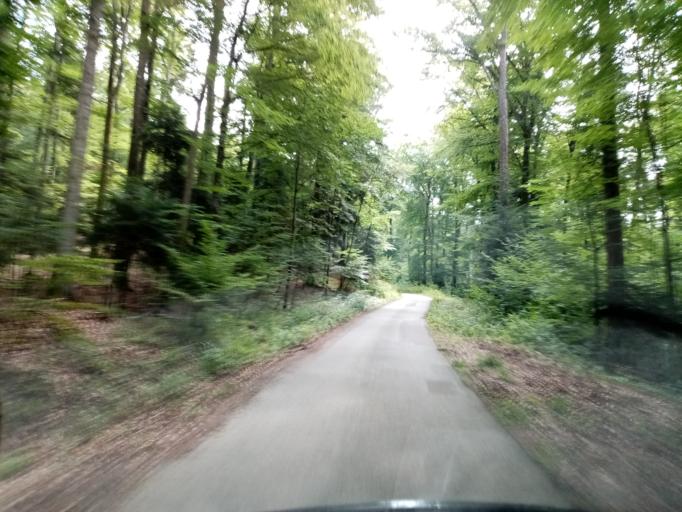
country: FR
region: Alsace
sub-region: Departement du Bas-Rhin
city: Ville
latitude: 48.3584
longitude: 7.3431
